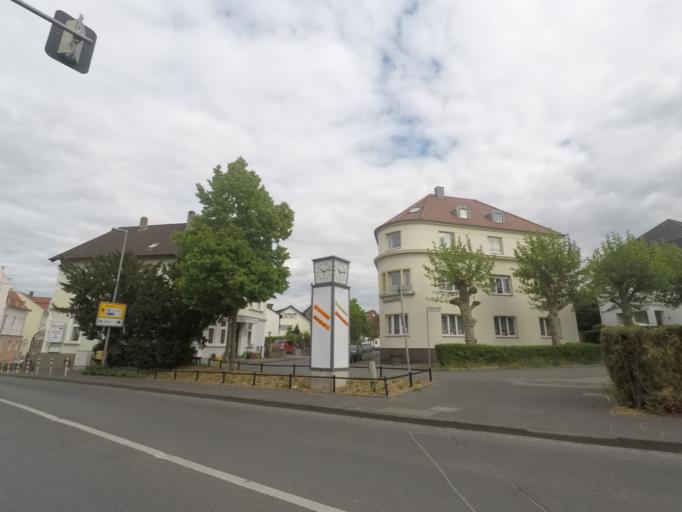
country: DE
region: North Rhine-Westphalia
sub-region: Regierungsbezirk Detmold
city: Bad Salzuflen
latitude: 52.0851
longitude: 8.7417
